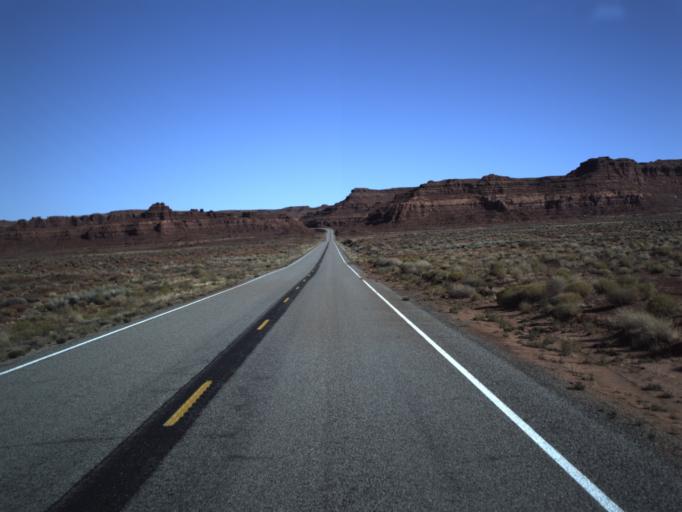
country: US
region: Utah
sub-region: San Juan County
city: Blanding
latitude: 37.8387
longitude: -110.3564
